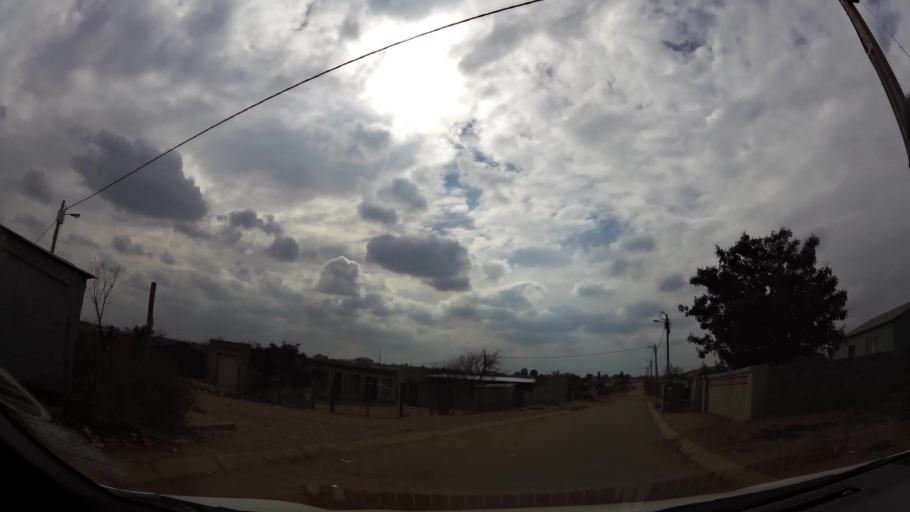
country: ZA
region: Gauteng
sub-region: Ekurhuleni Metropolitan Municipality
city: Germiston
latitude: -26.3886
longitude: 28.1313
